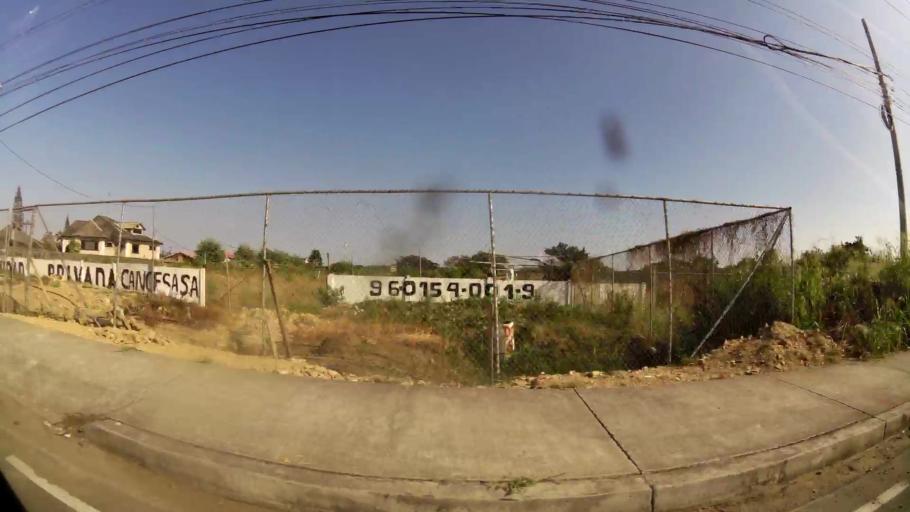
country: EC
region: Guayas
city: Santa Lucia
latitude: -2.1854
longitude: -79.9729
